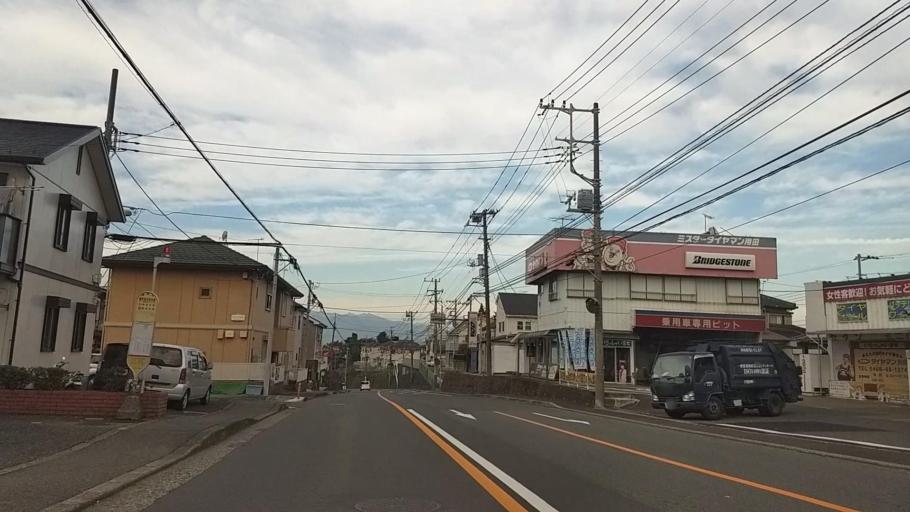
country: JP
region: Kanagawa
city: Atsugi
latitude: 35.4030
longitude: 139.4209
